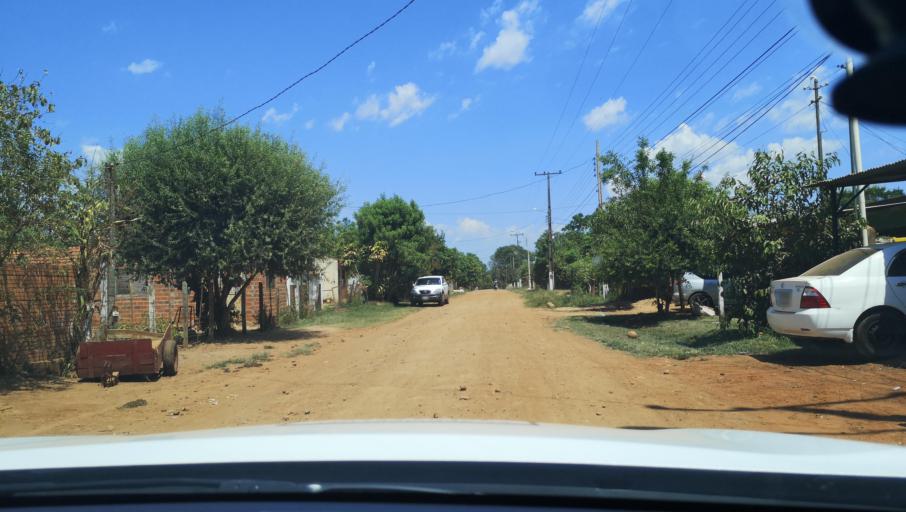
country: PY
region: Itapua
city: Carmen del Parana
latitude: -27.1619
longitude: -56.2265
